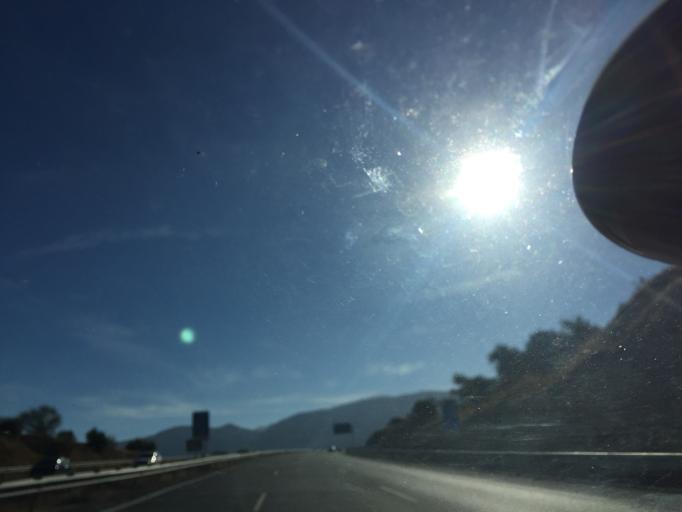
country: ES
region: Andalusia
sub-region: Provincia de Jaen
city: La Guardia de Jaen
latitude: 37.7603
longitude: -3.7114
